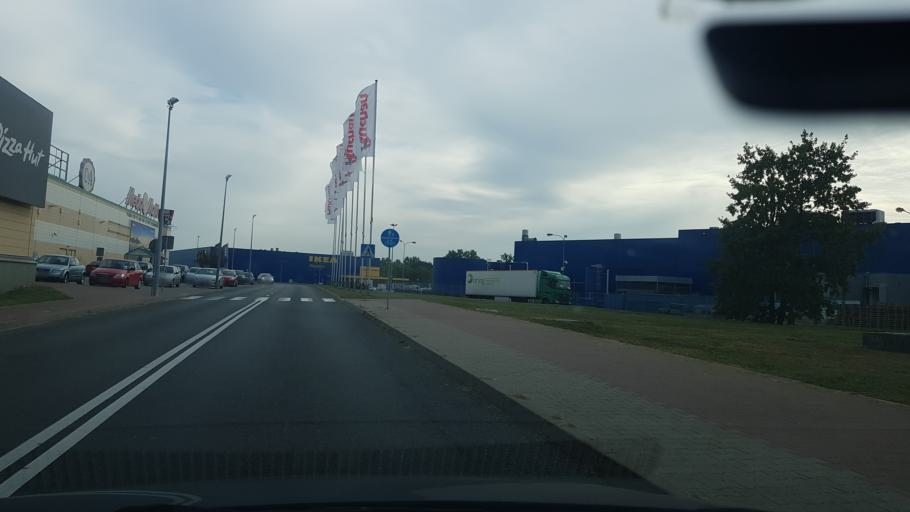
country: PL
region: Masovian Voivodeship
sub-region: Powiat wolominski
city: Marki
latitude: 52.3065
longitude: 21.0847
